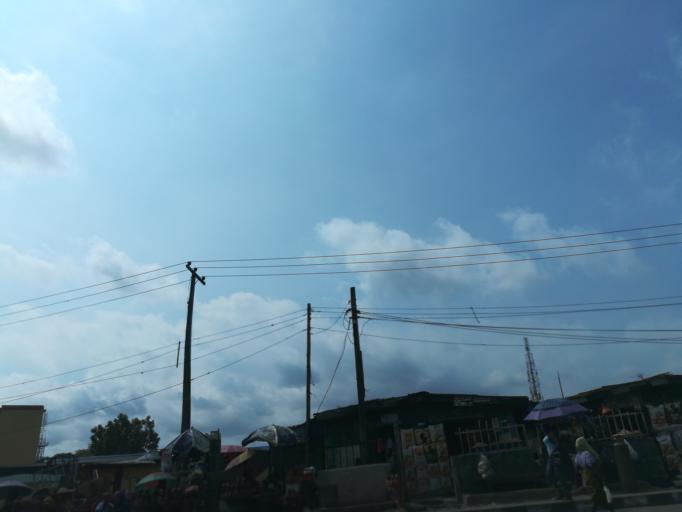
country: NG
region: Lagos
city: Lagos
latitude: 6.4549
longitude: 3.4035
